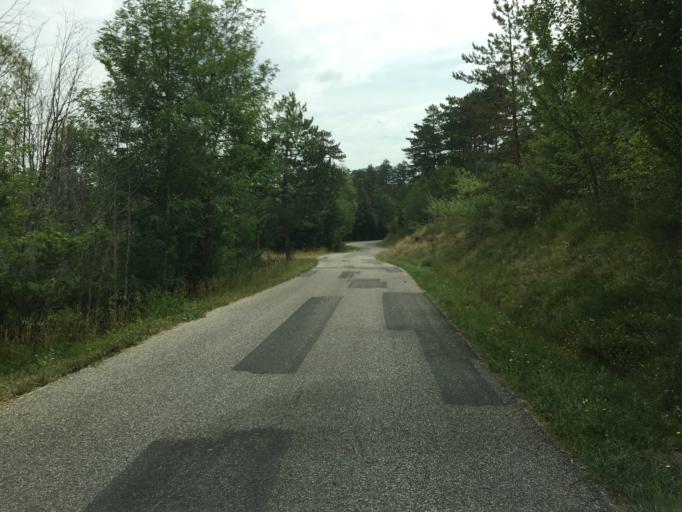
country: FR
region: Provence-Alpes-Cote d'Azur
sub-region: Departement des Alpes-de-Haute-Provence
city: Digne-les-Bains
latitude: 44.2172
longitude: 6.1425
